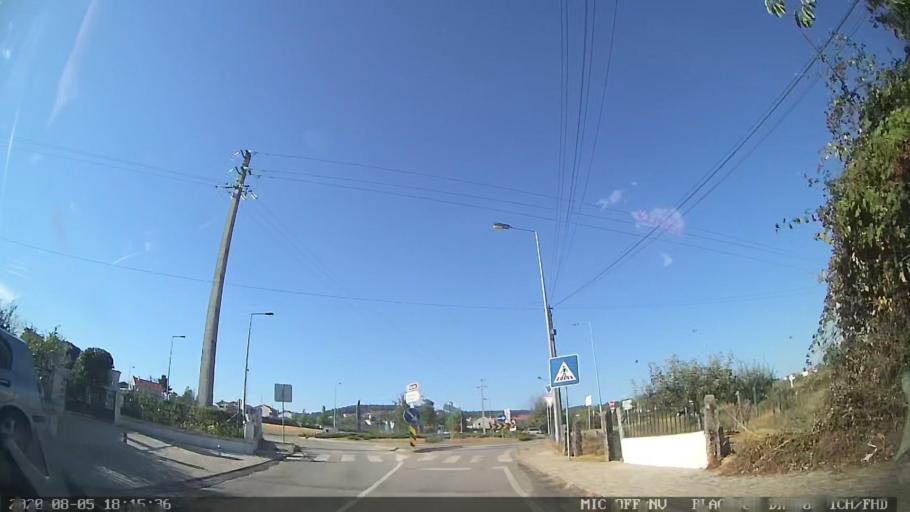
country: PT
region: Vila Real
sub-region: Sabrosa
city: Vilela
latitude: 41.2613
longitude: -7.6179
